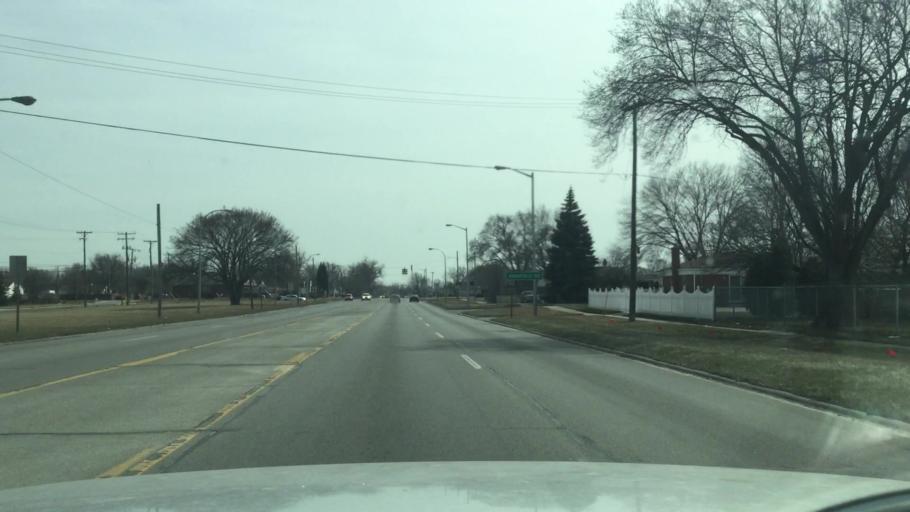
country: US
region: Michigan
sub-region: Wayne County
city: Inkster
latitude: 42.2768
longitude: -83.3289
